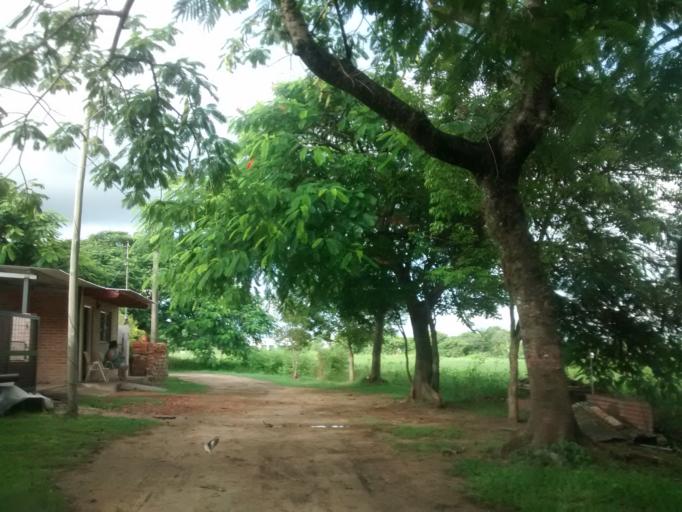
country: AR
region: Chaco
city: Puerto Tirol
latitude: -27.3761
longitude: -59.0892
